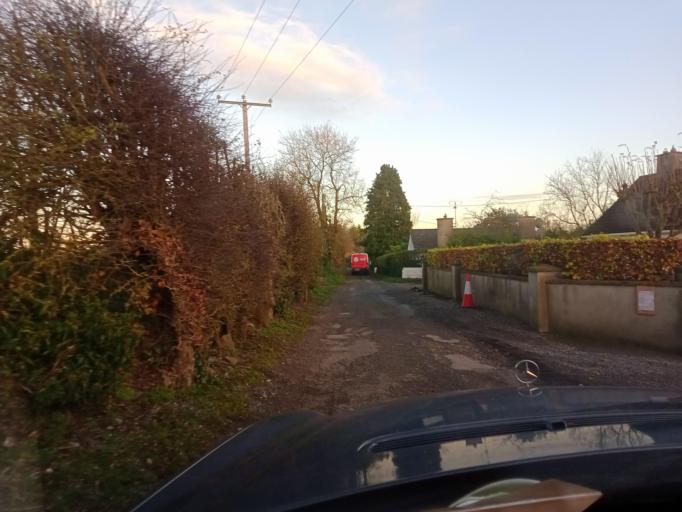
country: IE
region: Leinster
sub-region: Kilkenny
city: Kilkenny
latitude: 52.6105
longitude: -7.1926
